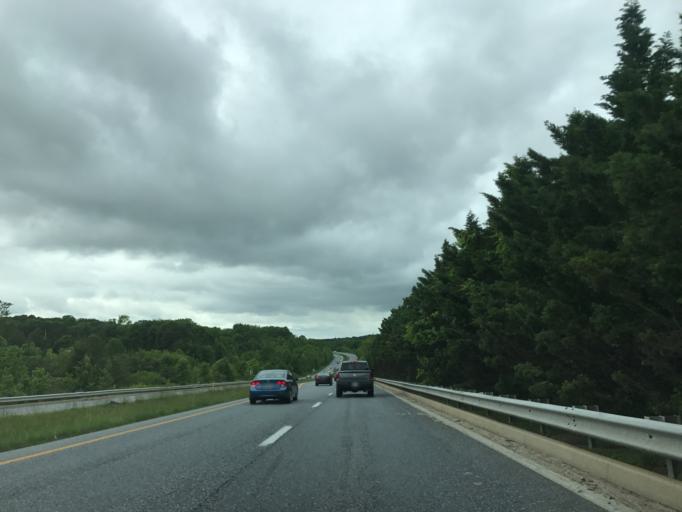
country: US
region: Maryland
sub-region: Prince George's County
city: Woodlawn
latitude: 38.9540
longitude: -76.8876
